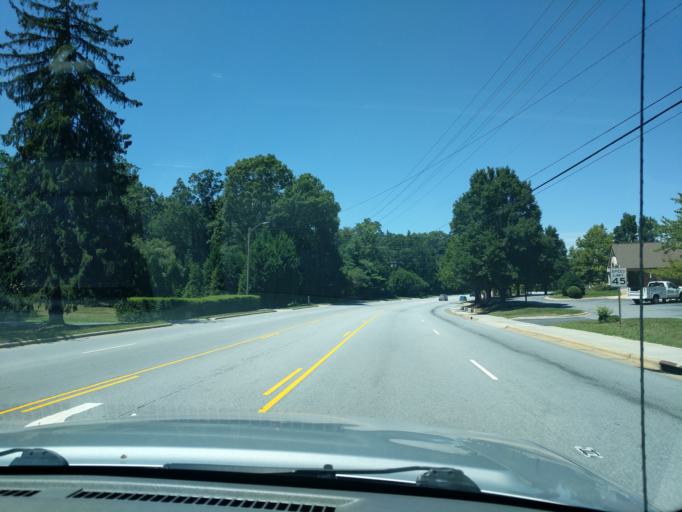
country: US
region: North Carolina
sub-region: Buncombe County
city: Biltmore Forest
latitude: 35.5392
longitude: -82.5312
